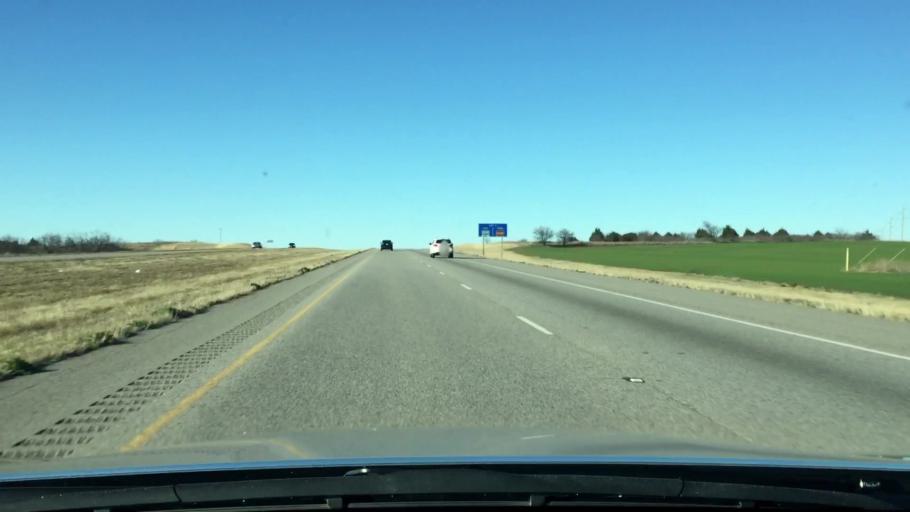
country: US
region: Texas
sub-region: Hill County
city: Itasca
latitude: 32.1389
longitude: -97.1217
